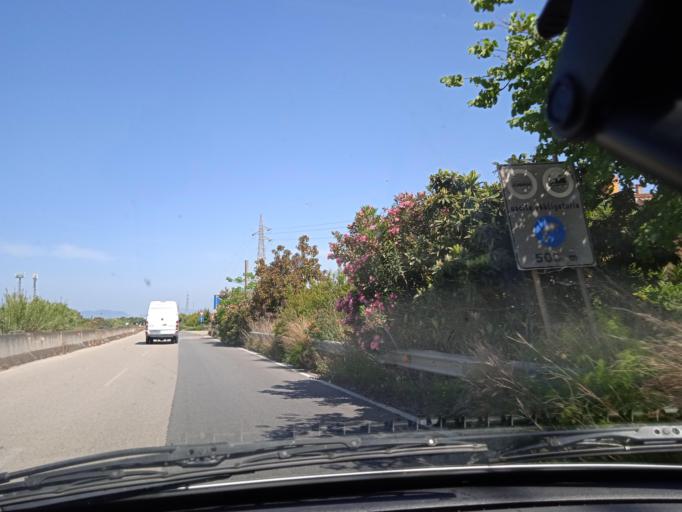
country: IT
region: Sicily
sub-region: Messina
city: Milazzo
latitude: 38.1936
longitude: 15.2580
